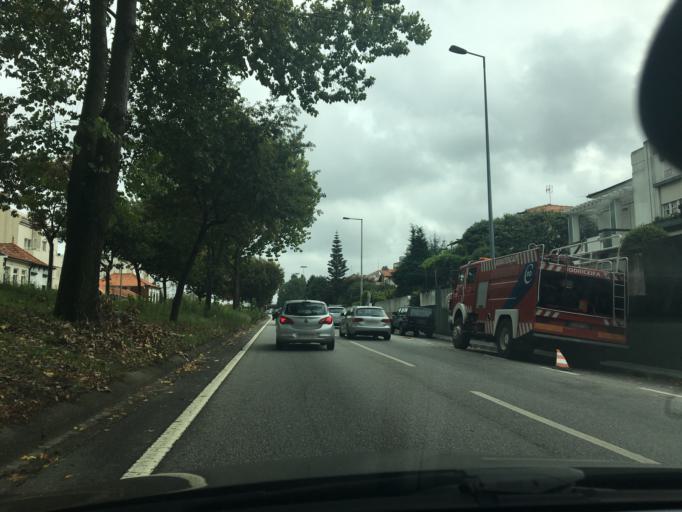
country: PT
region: Porto
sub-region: Matosinhos
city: Senhora da Hora
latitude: 41.1797
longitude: -8.6274
